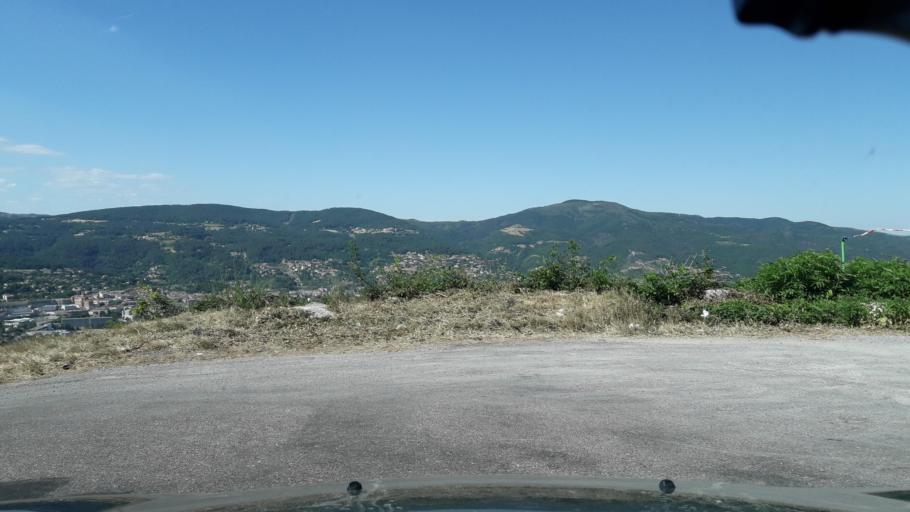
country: FR
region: Rhone-Alpes
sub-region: Departement de l'Ardeche
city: Privas
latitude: 44.7119
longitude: 4.6016
